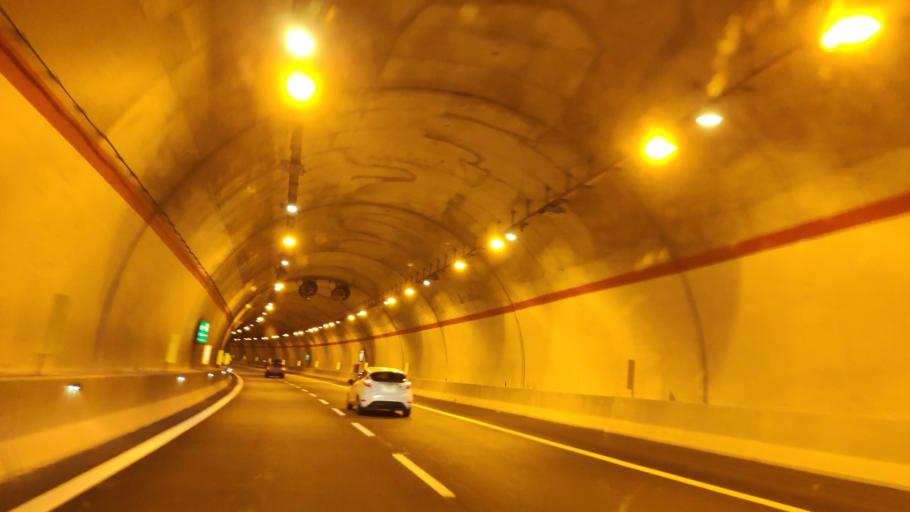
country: IT
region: Calabria
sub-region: Provincia di Cosenza
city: Laino Borgo
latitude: 39.9441
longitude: 15.9592
